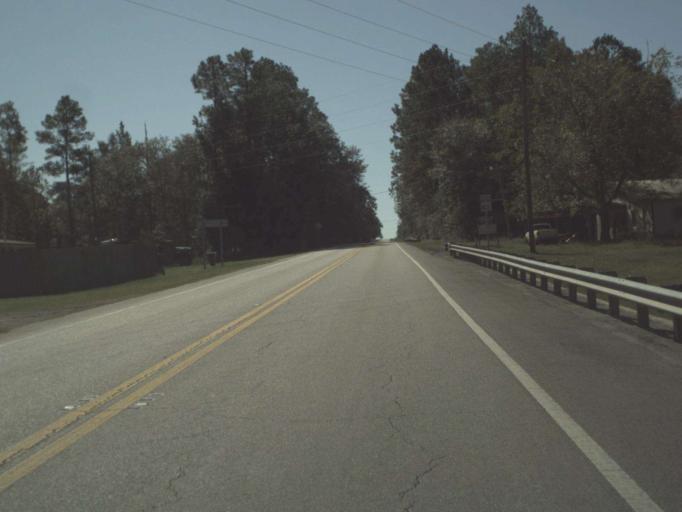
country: US
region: Alabama
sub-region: Geneva County
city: Samson
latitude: 30.9708
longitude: -86.1357
